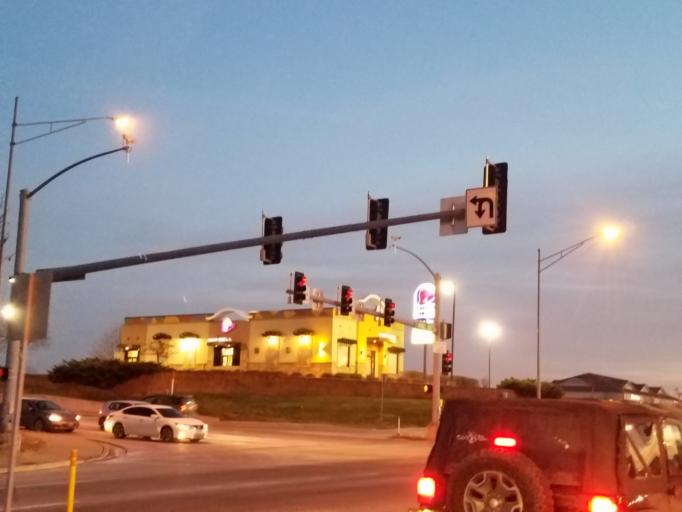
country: US
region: Missouri
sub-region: Boone County
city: Columbia
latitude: 38.9932
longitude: -92.3242
